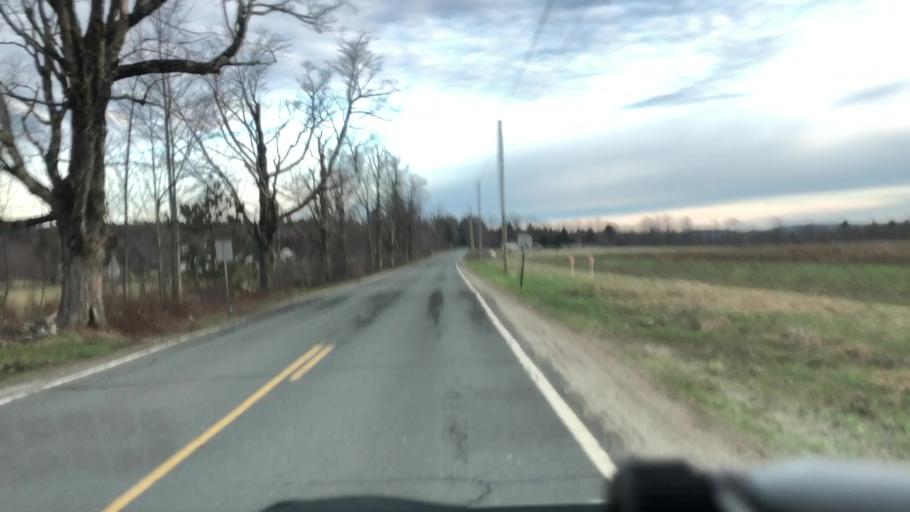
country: US
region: Massachusetts
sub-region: Hampshire County
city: Chesterfield
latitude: 42.4146
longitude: -72.9379
